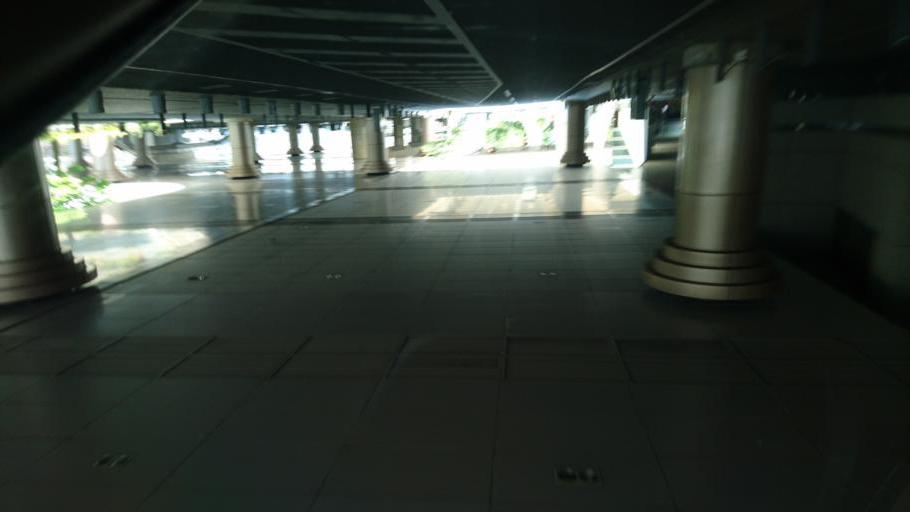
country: JP
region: Iwate
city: Morioka-shi
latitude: 39.7013
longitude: 141.1344
